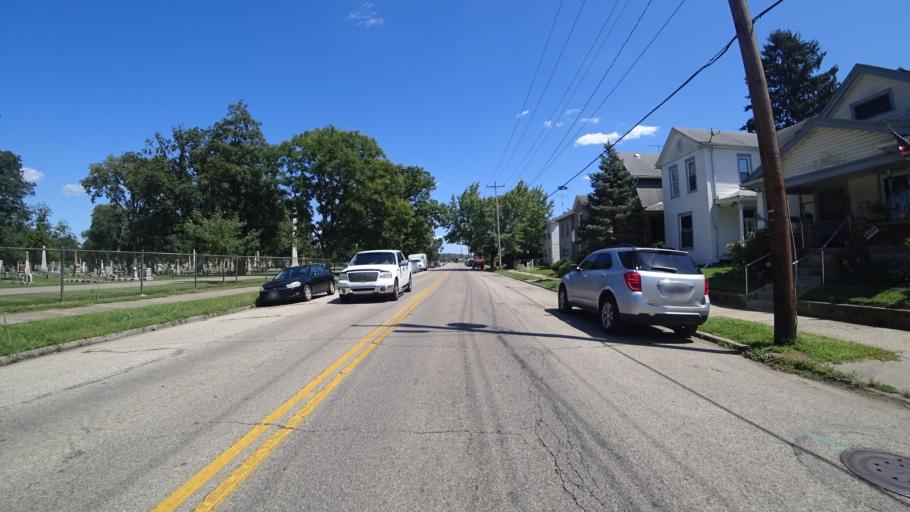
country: US
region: Ohio
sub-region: Butler County
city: Hamilton
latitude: 39.4011
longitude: -84.5447
